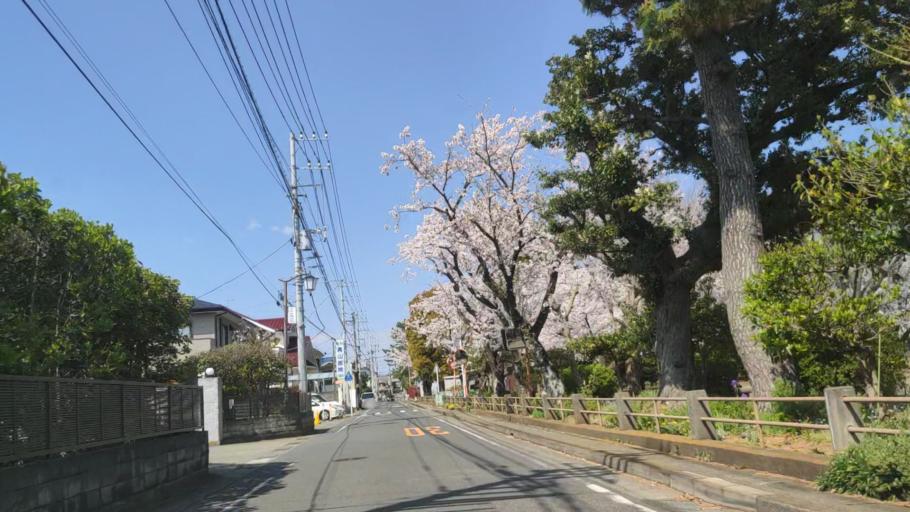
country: JP
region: Kanagawa
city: Hiratsuka
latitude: 35.3350
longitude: 139.3311
